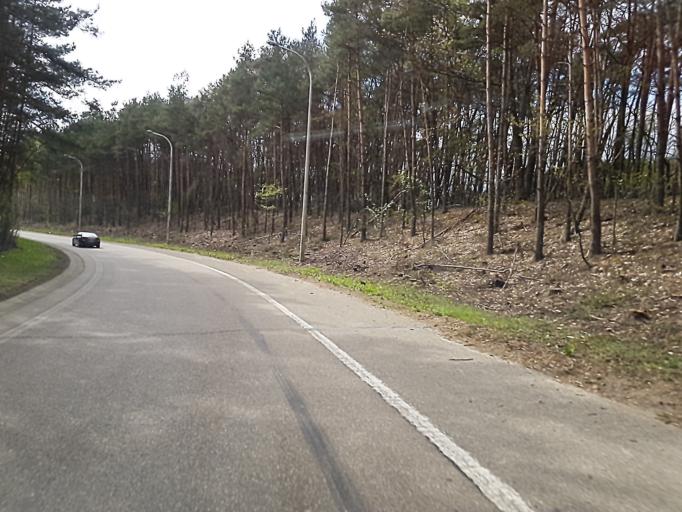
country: BE
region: Flanders
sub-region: Provincie Limburg
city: As
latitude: 50.9797
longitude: 5.5475
